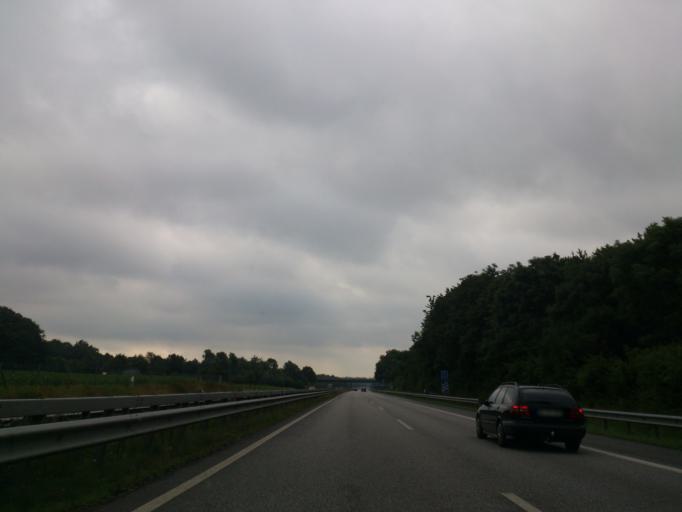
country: DE
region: Schleswig-Holstein
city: Agethorst
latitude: 54.0325
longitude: 9.4375
